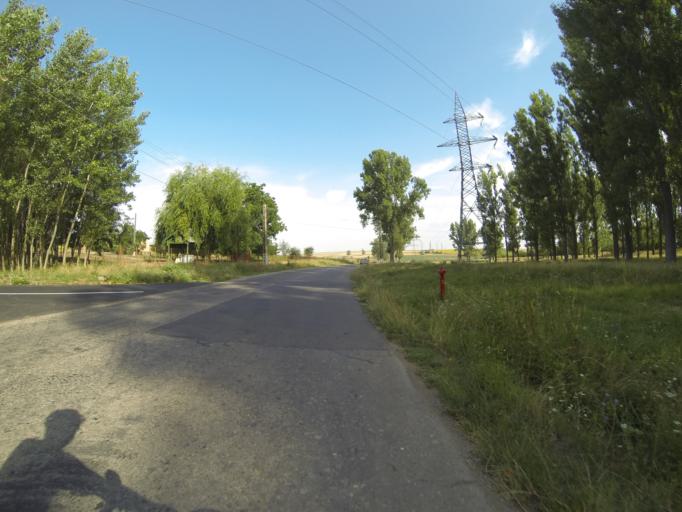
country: RO
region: Dolj
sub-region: Comuna Dranicu
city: Padea
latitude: 44.0306
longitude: 23.8591
